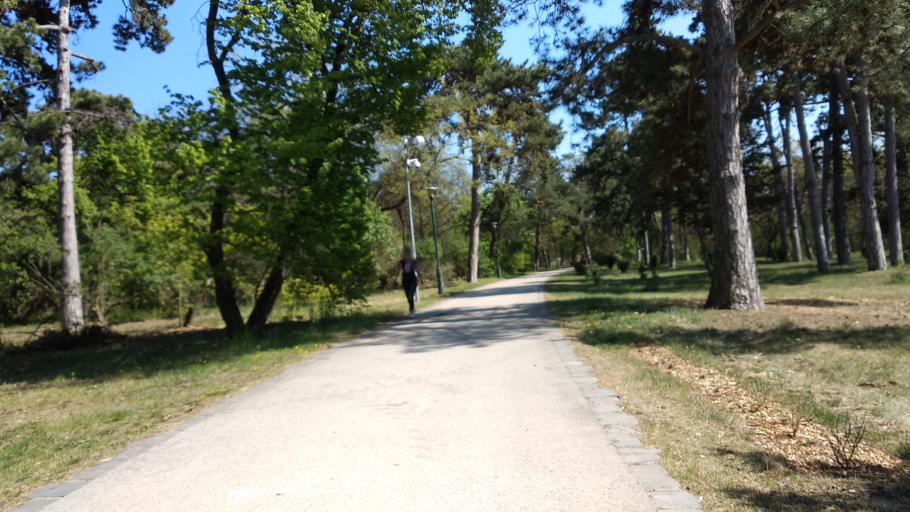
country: HU
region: Pest
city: Godollo
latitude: 47.5944
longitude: 19.3546
